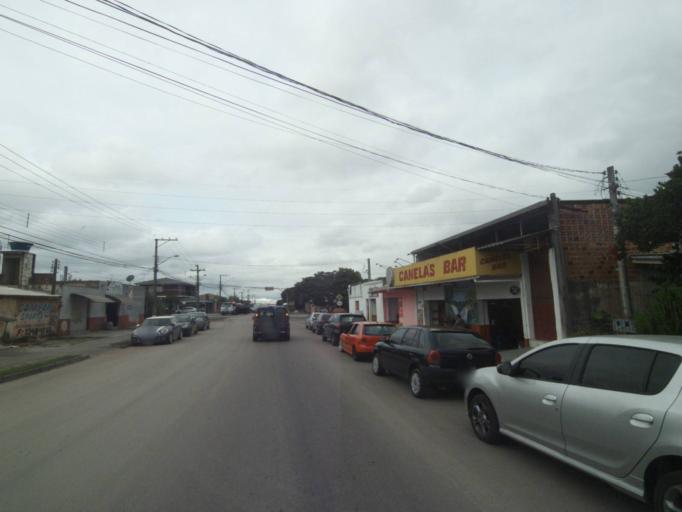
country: BR
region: Parana
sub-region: Sao Jose Dos Pinhais
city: Sao Jose dos Pinhais
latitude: -25.5422
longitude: -49.2745
